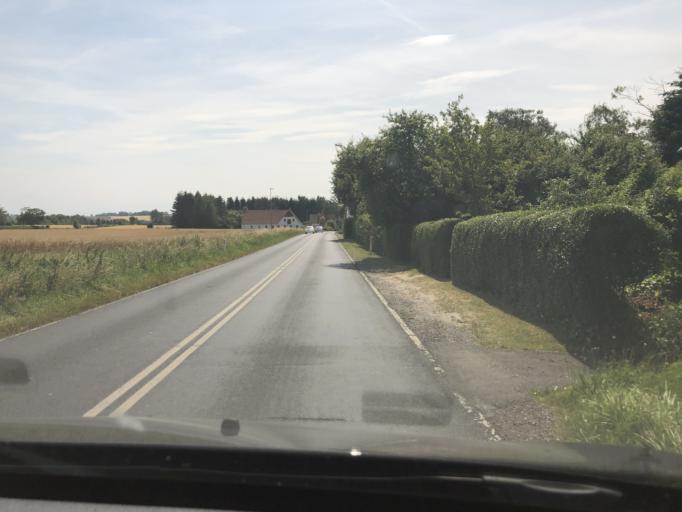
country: DK
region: South Denmark
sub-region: AEro Kommune
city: AEroskobing
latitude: 54.8817
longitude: 10.4030
